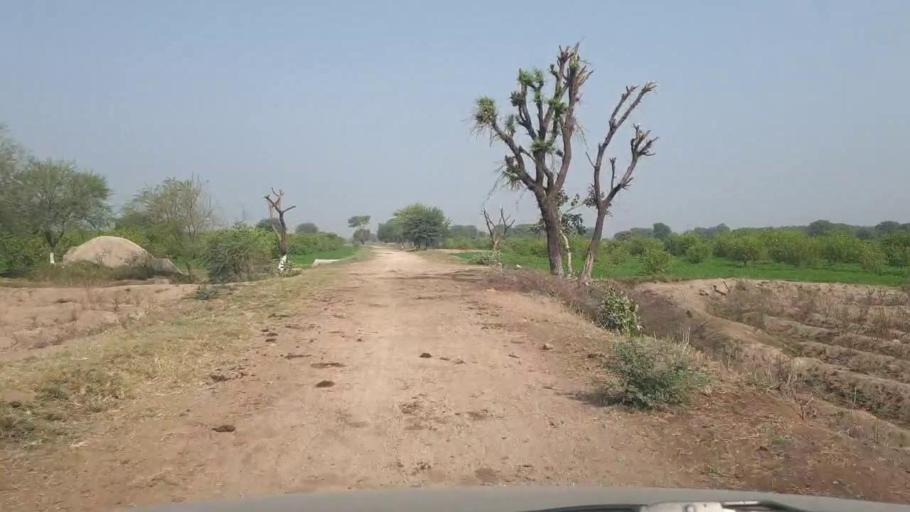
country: PK
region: Sindh
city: Umarkot
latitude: 25.3925
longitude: 69.7100
